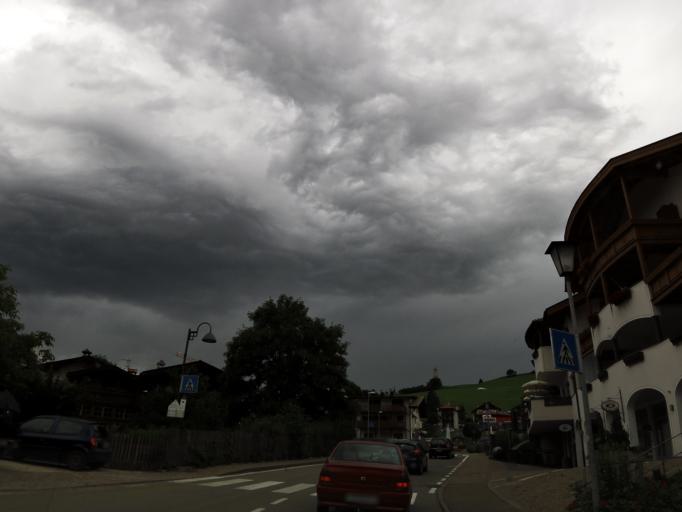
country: IT
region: Trentino-Alto Adige
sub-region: Bolzano
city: Siusi
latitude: 46.5438
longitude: 11.5621
